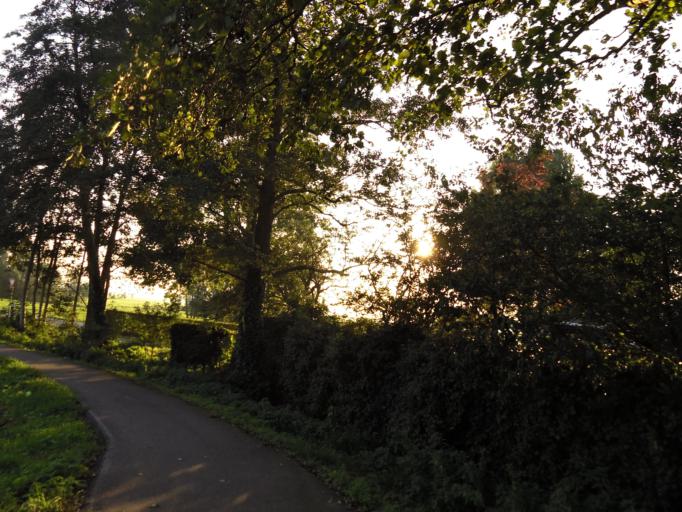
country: NL
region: South Holland
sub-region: Gemeente Kaag en Braassem
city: Oude Wetering
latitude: 52.1679
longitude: 4.6035
